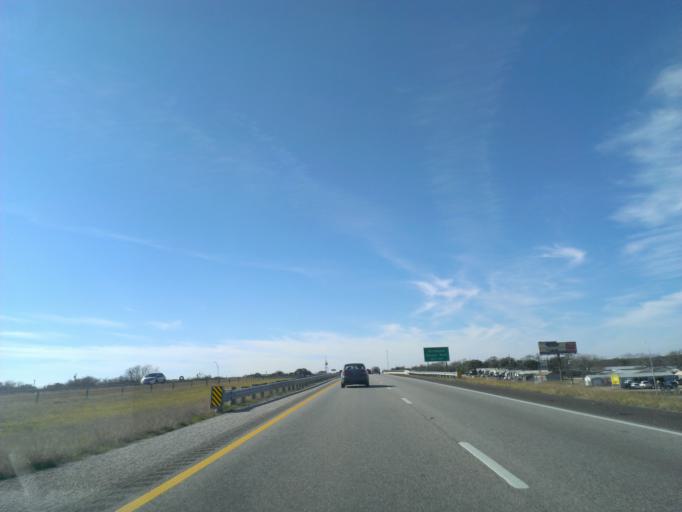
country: US
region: Texas
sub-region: Bell County
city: Belton
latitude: 31.0558
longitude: -97.5318
